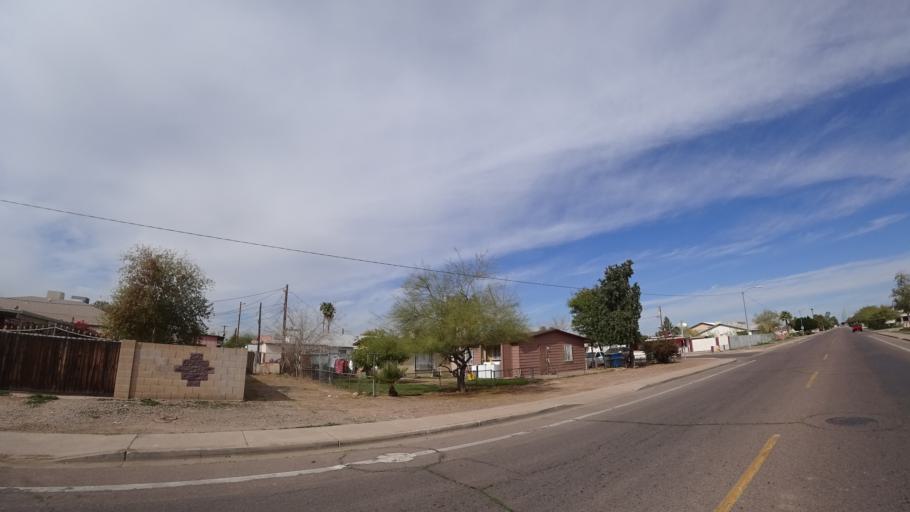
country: US
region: Arizona
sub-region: Maricopa County
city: Phoenix
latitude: 33.4677
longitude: -112.1258
